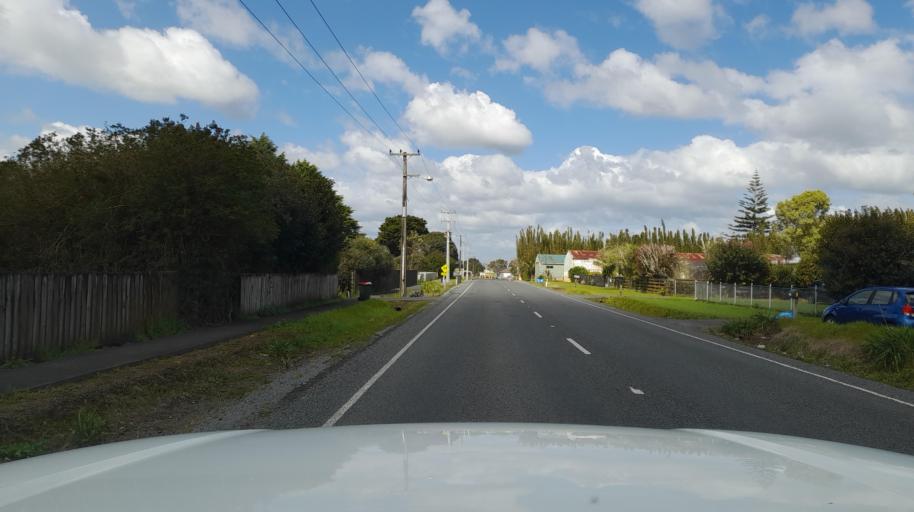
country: NZ
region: Northland
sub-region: Far North District
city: Waimate North
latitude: -35.3503
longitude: 173.8798
